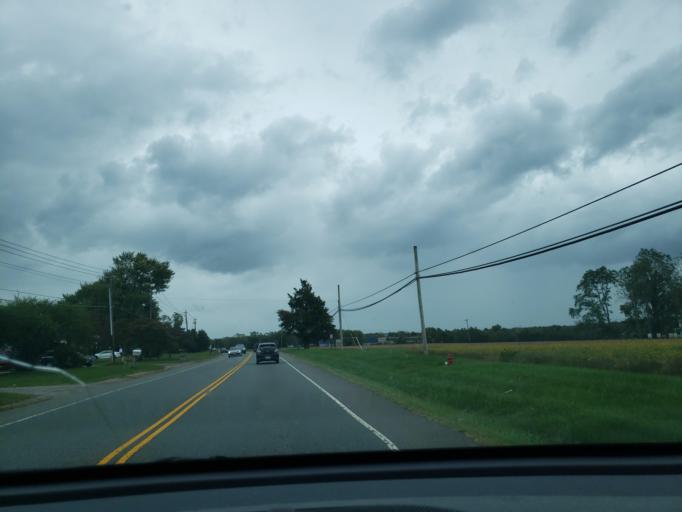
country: US
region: Virginia
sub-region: City of Fredericksburg
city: Fredericksburg
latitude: 38.2659
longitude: -77.4411
